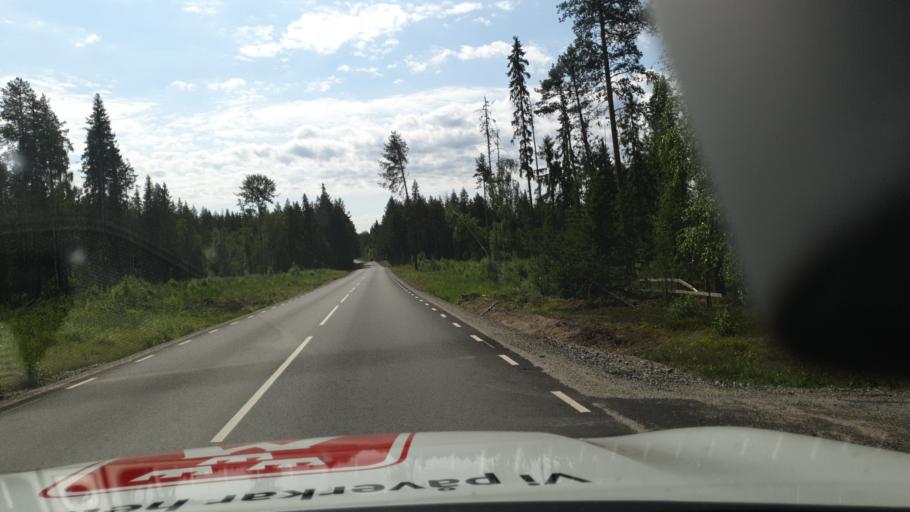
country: SE
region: Vaesterbotten
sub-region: Norsjo Kommun
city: Norsjoe
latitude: 64.6516
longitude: 19.2762
